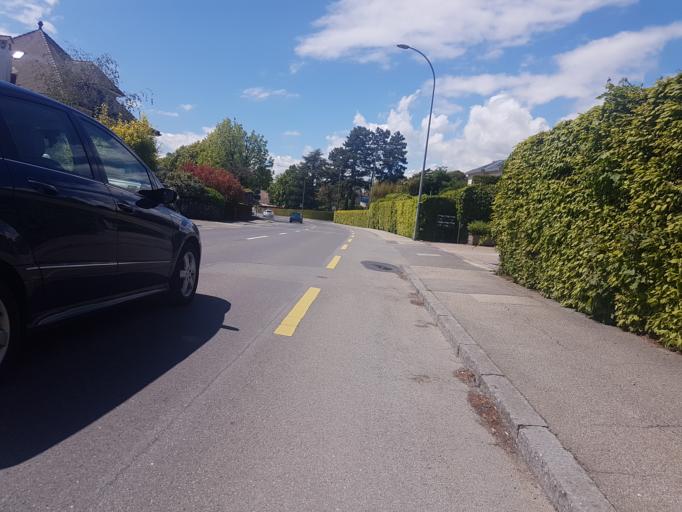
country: CH
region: Vaud
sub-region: Nyon District
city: Prangins
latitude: 46.3877
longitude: 6.2475
